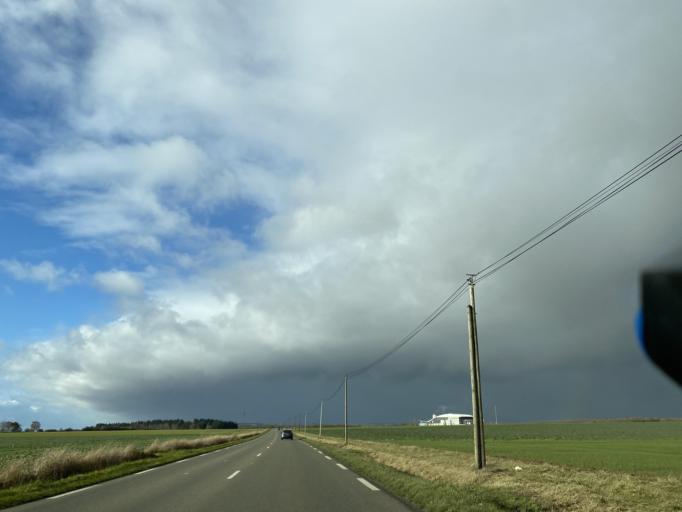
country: FR
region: Centre
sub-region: Departement d'Eure-et-Loir
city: Mainvilliers
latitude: 48.4597
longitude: 1.4420
